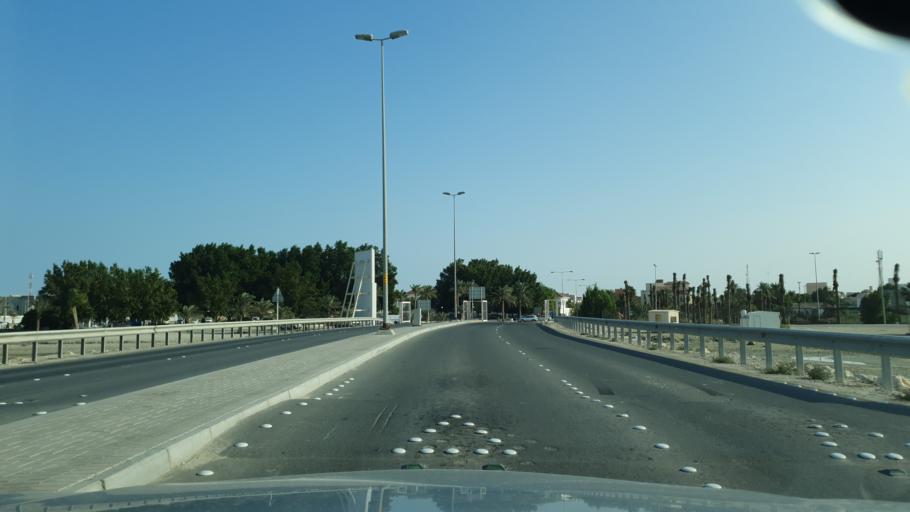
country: BH
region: Manama
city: Jidd Hafs
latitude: 26.2251
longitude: 50.4588
